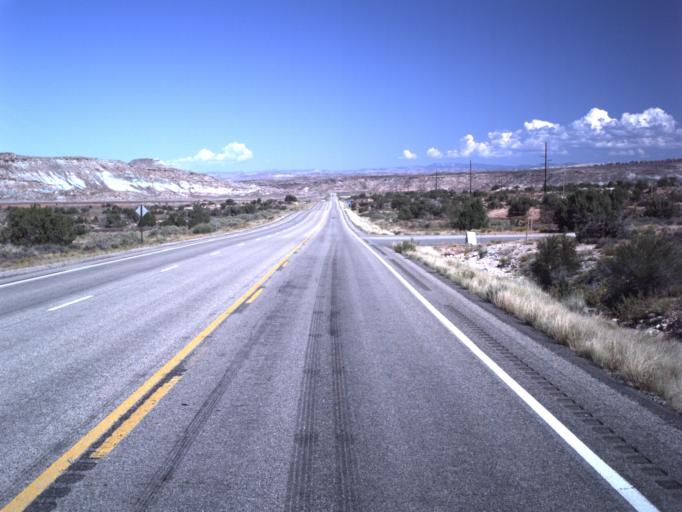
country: US
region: Utah
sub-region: Grand County
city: Moab
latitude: 38.6864
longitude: -109.6955
